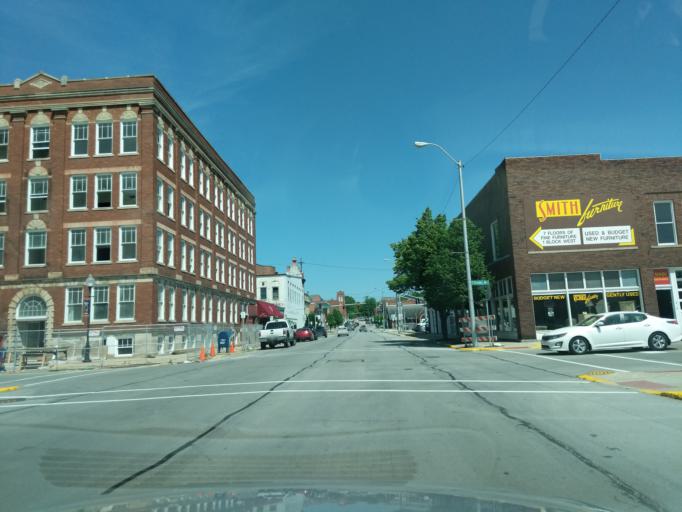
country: US
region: Indiana
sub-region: Huntington County
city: Huntington
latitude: 40.8816
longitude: -85.4930
